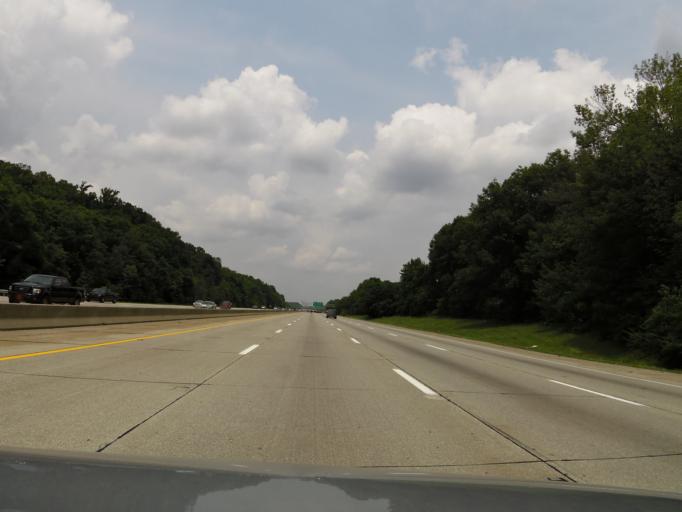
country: US
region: Kentucky
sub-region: Jefferson County
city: Heritage Creek
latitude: 38.1014
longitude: -85.7009
